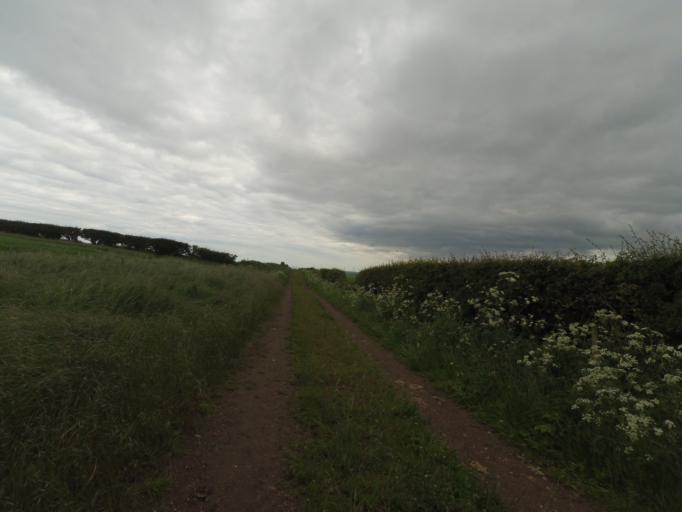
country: GB
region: Scotland
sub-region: East Lothian
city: Prestonpans
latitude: 55.9225
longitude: -2.9923
